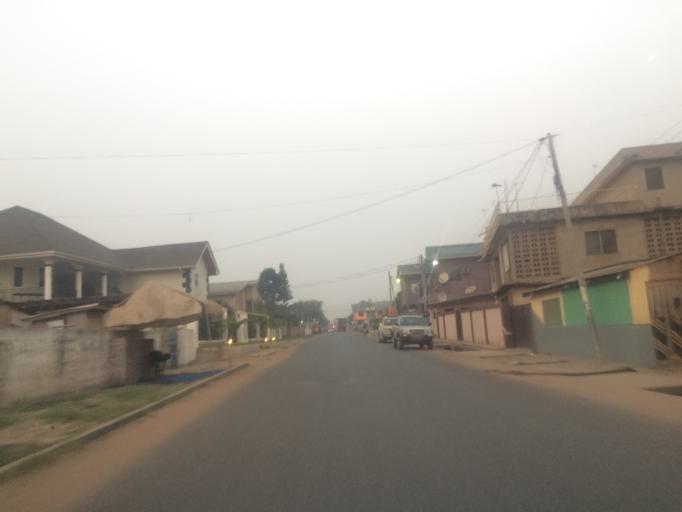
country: GH
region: Greater Accra
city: Nungua
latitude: 5.6002
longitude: -0.0954
